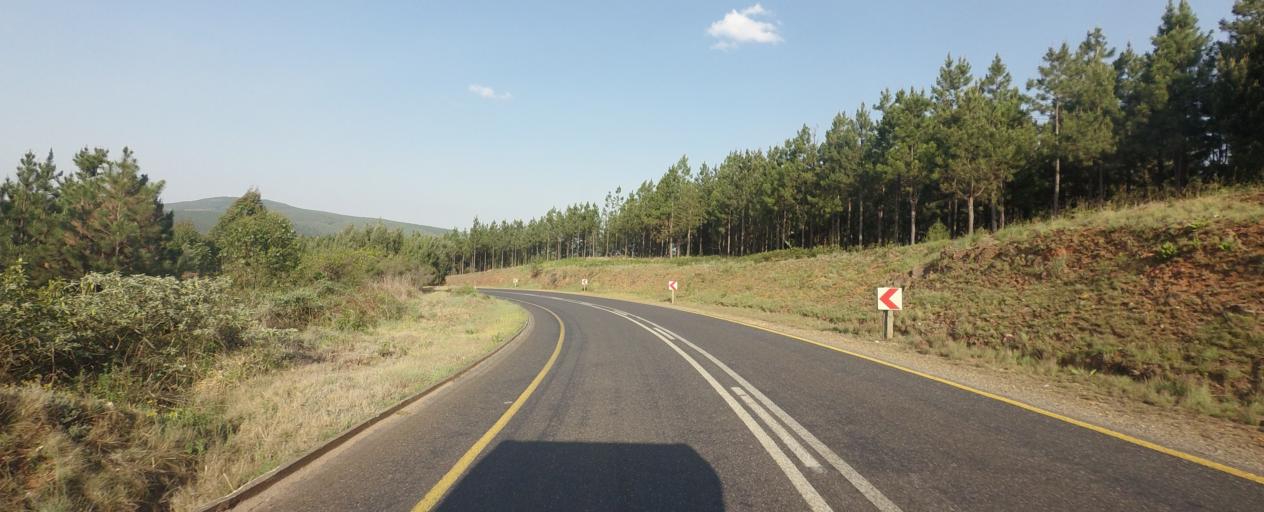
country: ZA
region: Mpumalanga
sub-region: Ehlanzeni District
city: Graksop
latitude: -25.1789
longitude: 30.7105
